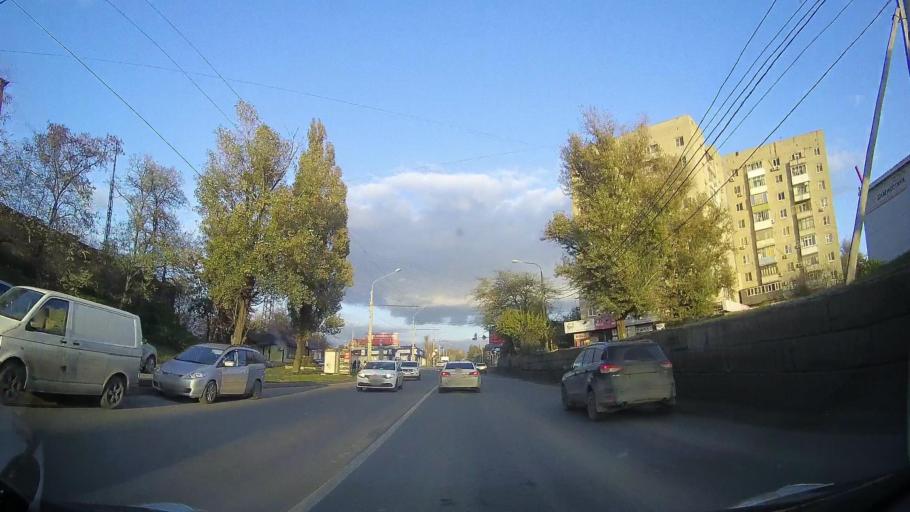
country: RU
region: Rostov
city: Imeni Chkalova
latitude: 47.2636
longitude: 39.7754
